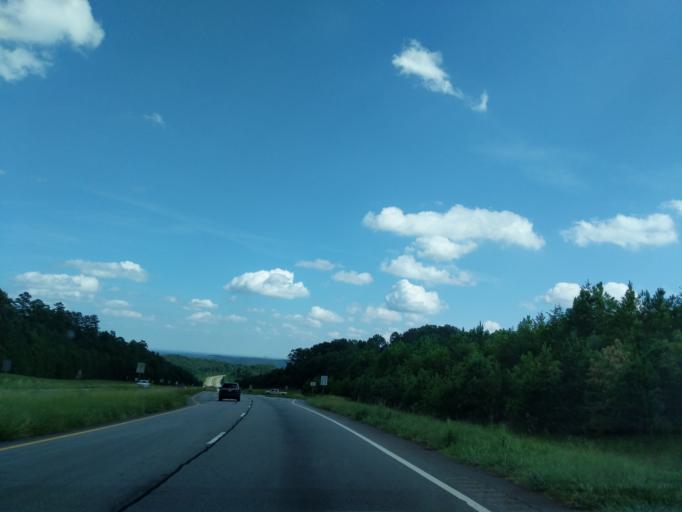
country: US
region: Georgia
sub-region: Habersham County
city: Baldwin
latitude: 34.4869
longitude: -83.5314
